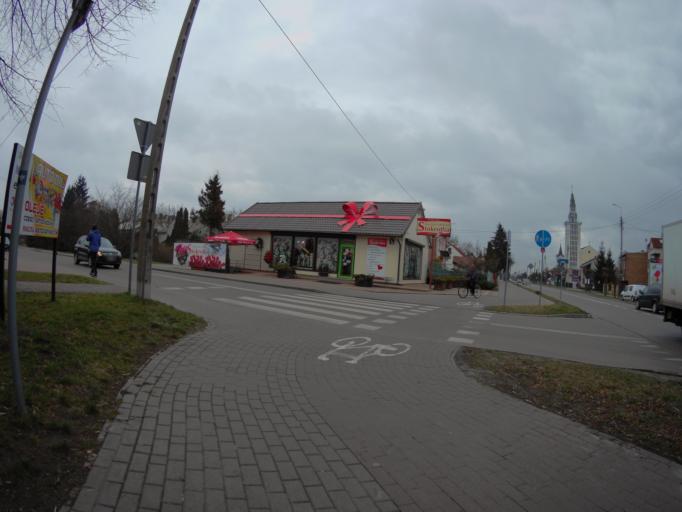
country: PL
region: Lublin Voivodeship
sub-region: Powiat bialski
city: Terespol
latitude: 52.0736
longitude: 23.6095
